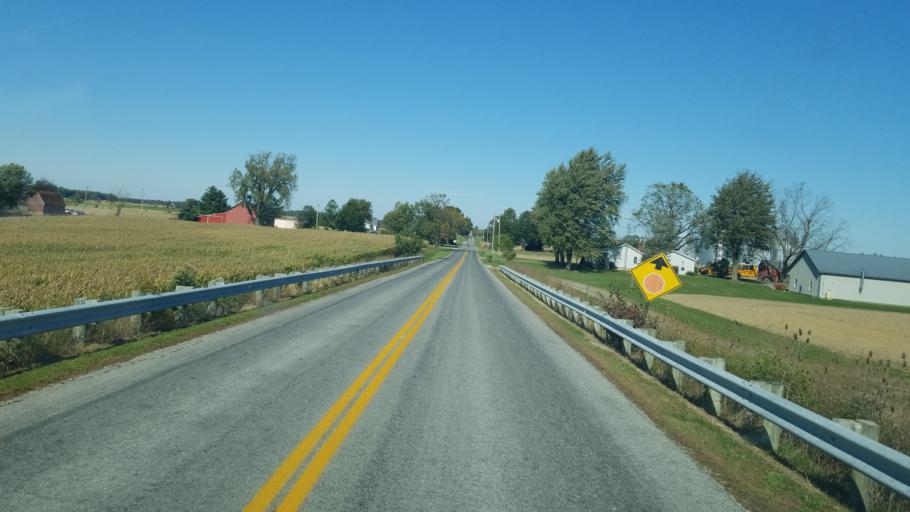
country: US
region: Ohio
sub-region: Huron County
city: Greenwich
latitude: 41.0506
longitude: -82.5853
